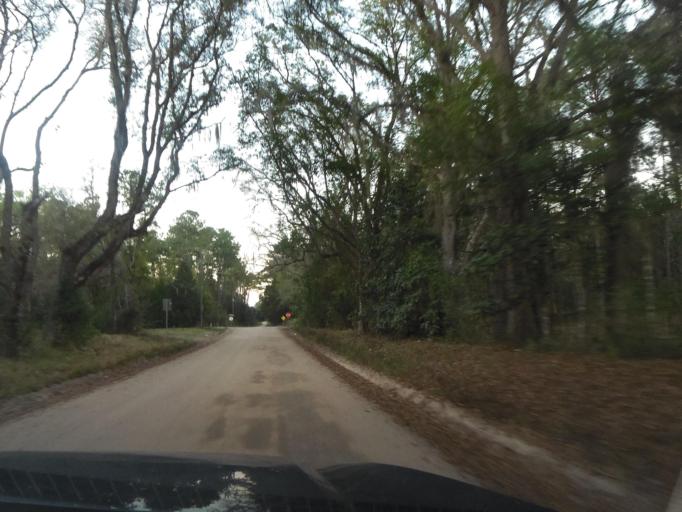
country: US
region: Florida
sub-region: Clay County
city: Asbury Lake
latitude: 29.9819
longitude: -81.7942
